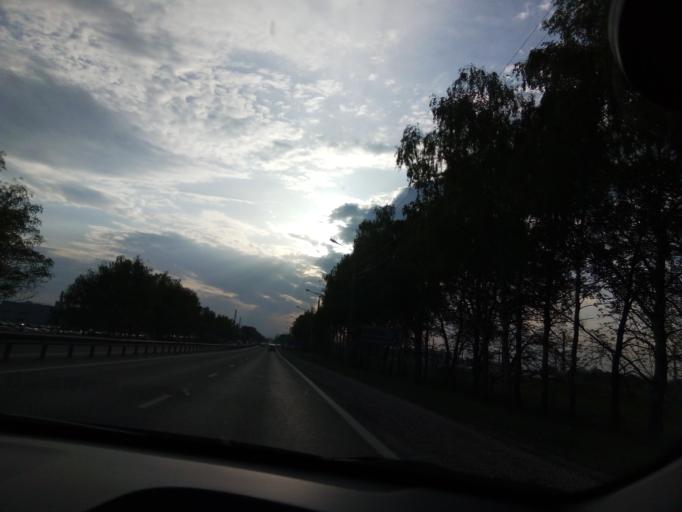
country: RU
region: Chuvashia
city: Novocheboksarsk
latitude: 56.1254
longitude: 47.3694
